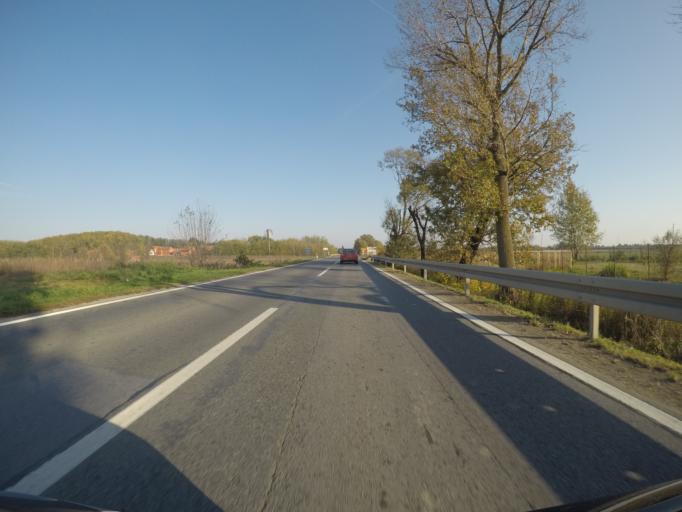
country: HR
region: Virovitick-Podravska
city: Pitomaca
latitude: 45.9655
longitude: 17.2089
